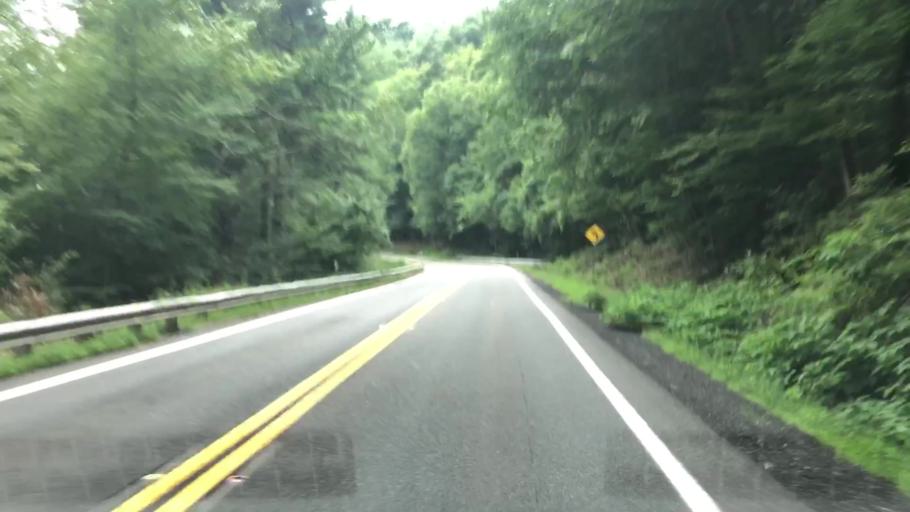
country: US
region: Massachusetts
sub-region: Hampshire County
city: Westhampton
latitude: 42.2998
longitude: -72.8650
